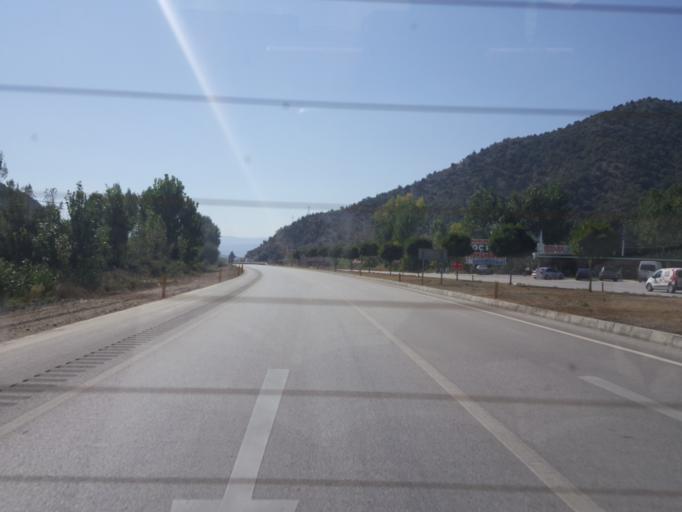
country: TR
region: Corum
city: Osmancik
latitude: 40.9753
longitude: 34.9140
